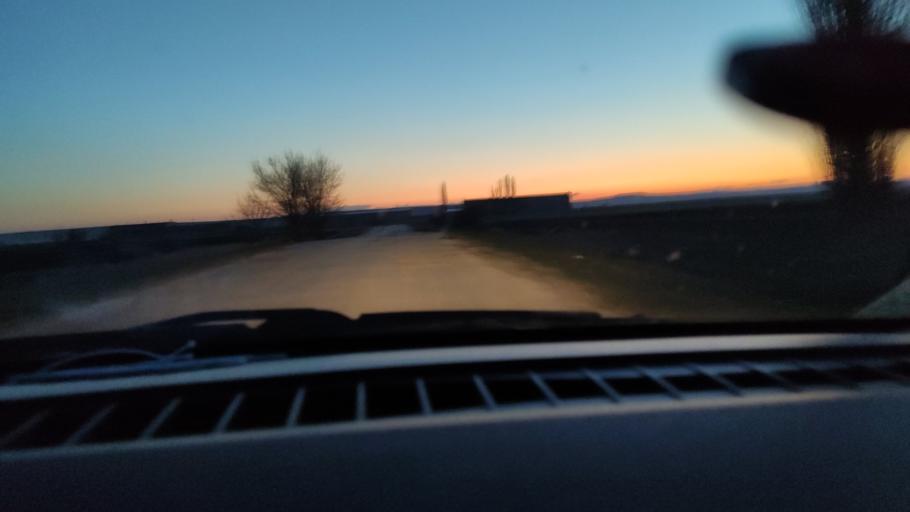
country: RU
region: Saratov
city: Rovnoye
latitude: 50.9380
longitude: 46.0967
